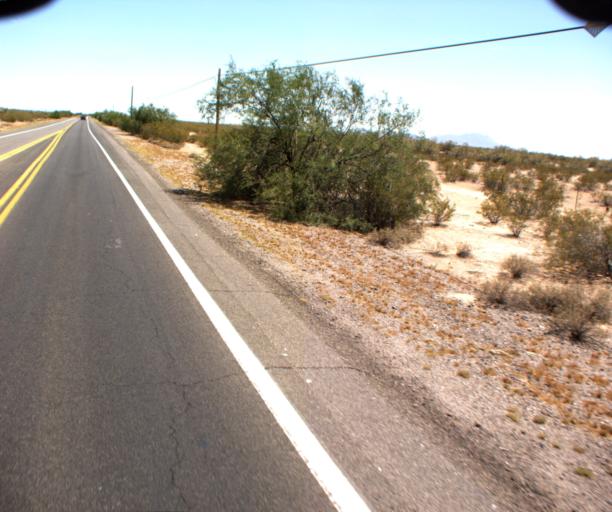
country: US
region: Arizona
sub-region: Pinal County
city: Florence
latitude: 33.0015
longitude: -111.3710
